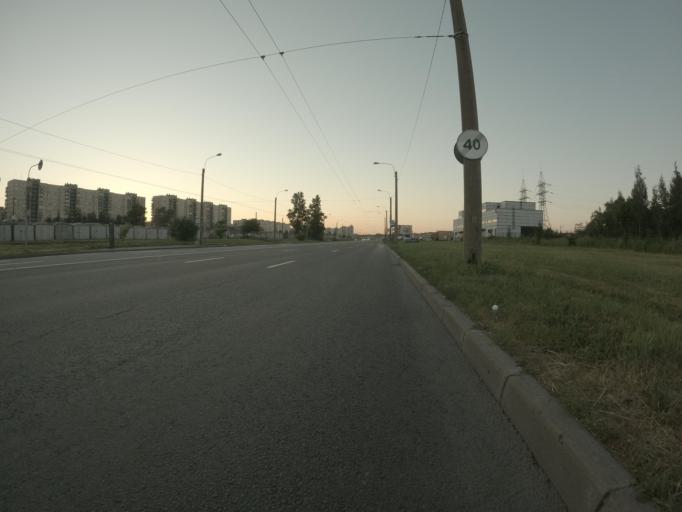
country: RU
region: St.-Petersburg
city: Krasnogvargeisky
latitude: 59.9360
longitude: 30.5037
